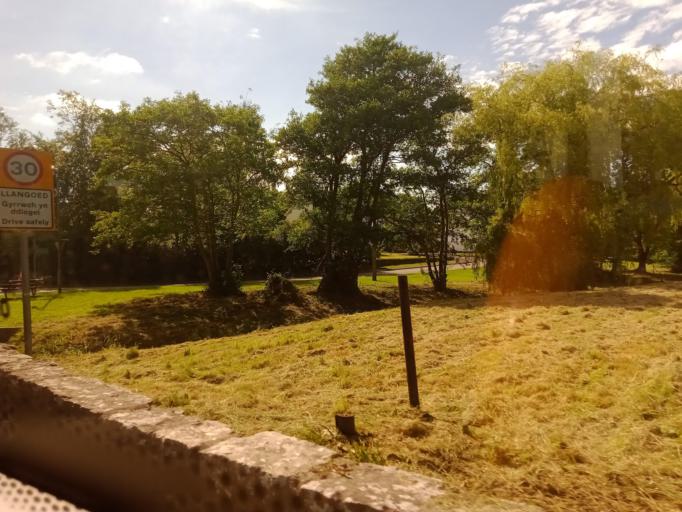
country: GB
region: Wales
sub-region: Anglesey
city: Llangoed
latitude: 53.2960
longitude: -4.0861
